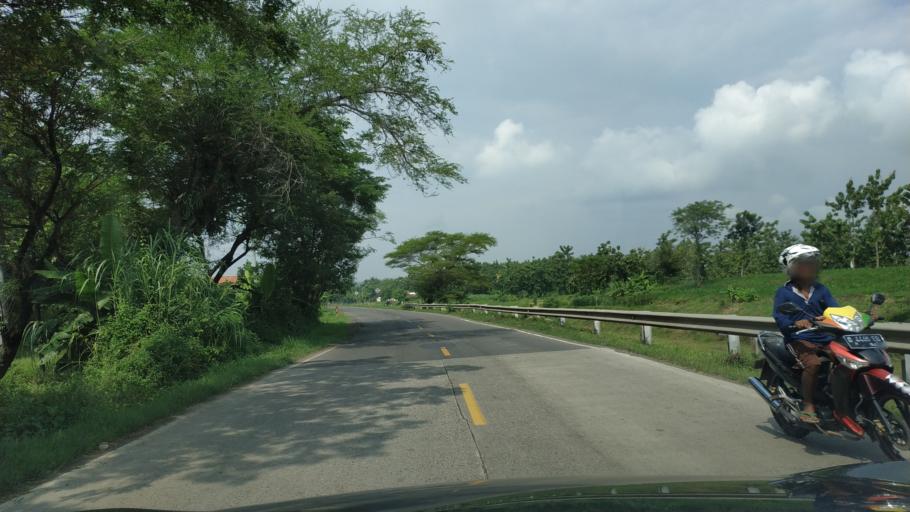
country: ID
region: Central Java
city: Margasari
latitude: -7.0699
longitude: 108.9837
